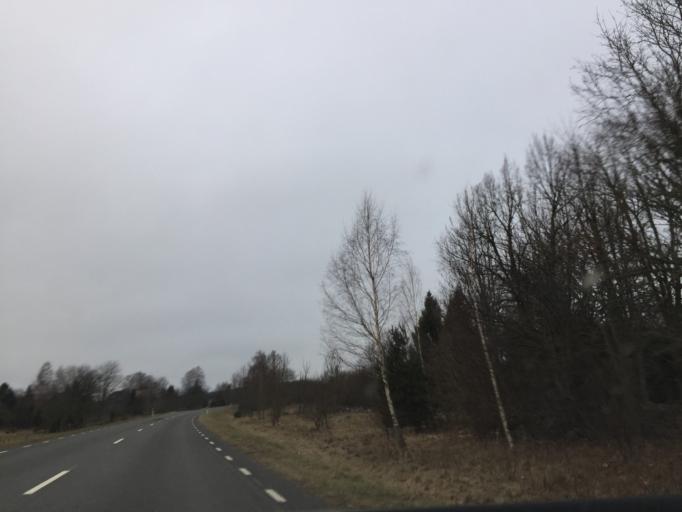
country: EE
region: Saare
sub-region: Kuressaare linn
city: Kuressaare
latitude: 58.5380
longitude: 22.3381
